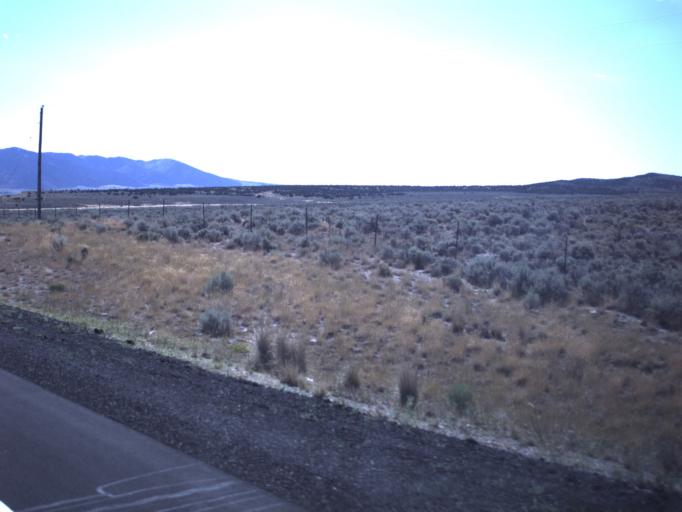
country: US
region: Utah
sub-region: Utah County
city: Eagle Mountain
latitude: 40.0760
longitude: -112.3436
